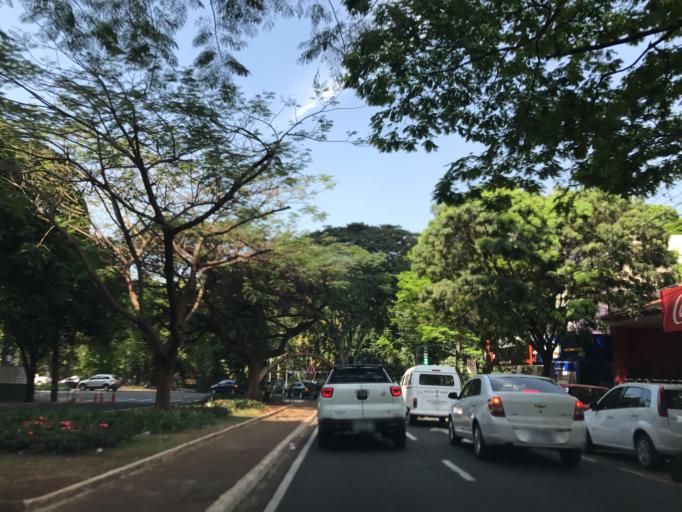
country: BR
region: Parana
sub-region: Maringa
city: Maringa
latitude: -23.4258
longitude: -51.9340
